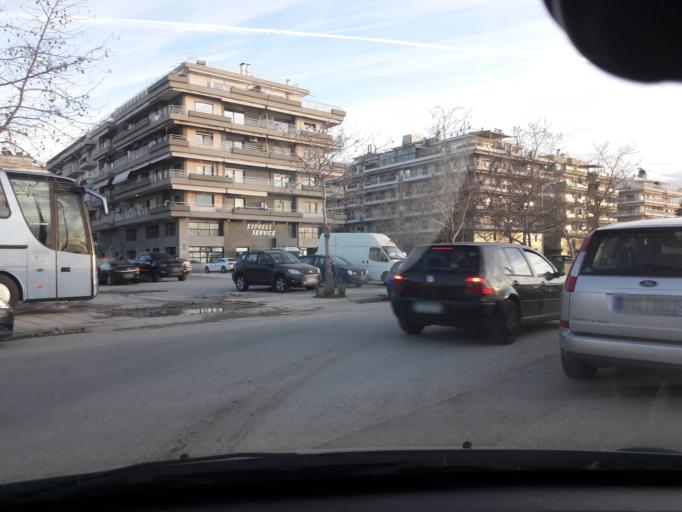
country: GR
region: Central Macedonia
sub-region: Nomos Thessalonikis
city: Kalamaria
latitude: 40.5943
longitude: 22.9494
